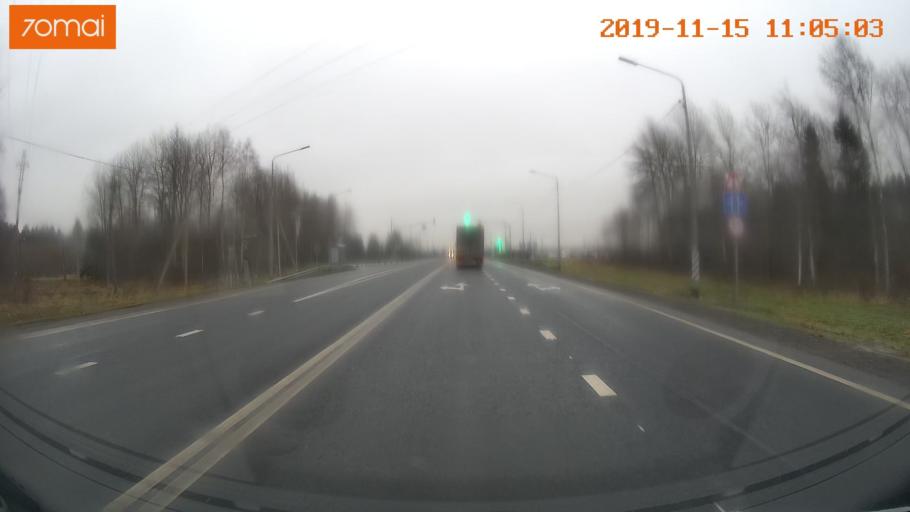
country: RU
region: Vologda
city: Chebsara
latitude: 59.1184
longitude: 38.9970
